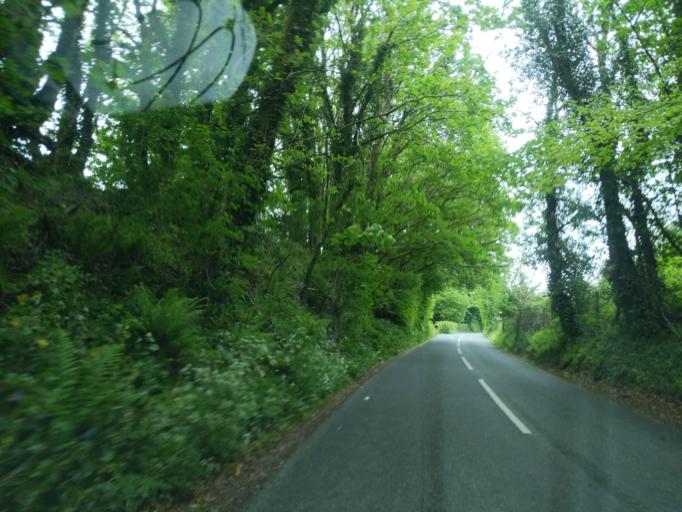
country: GB
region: England
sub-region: Devon
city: Tavistock
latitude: 50.6297
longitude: -4.1186
